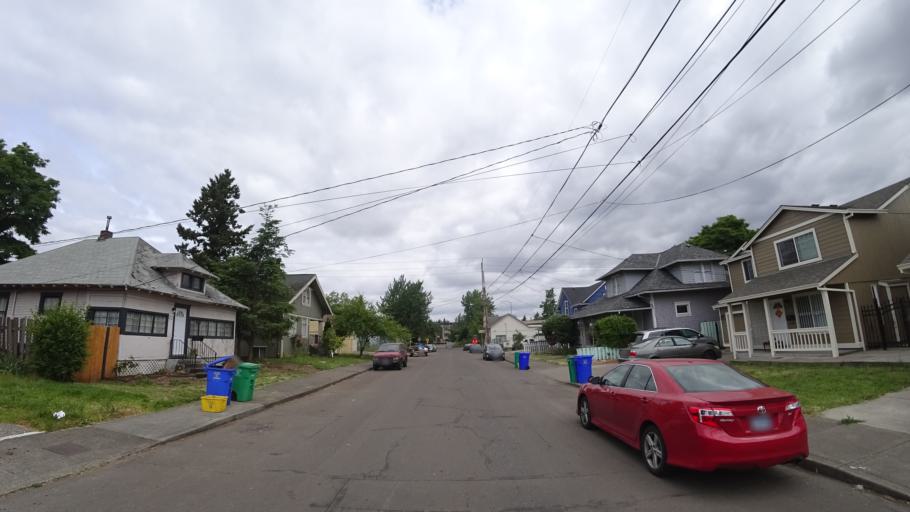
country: US
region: Oregon
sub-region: Multnomah County
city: Lents
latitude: 45.4784
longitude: -122.5706
